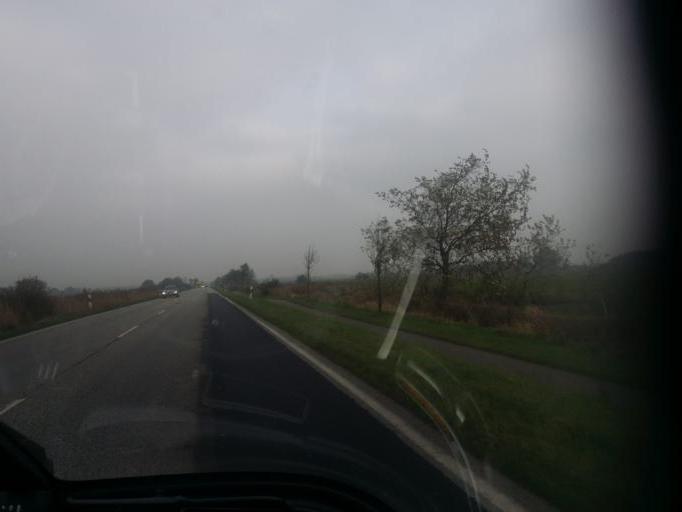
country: DE
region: Schleswig-Holstein
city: Hattstedtermarsch
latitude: 54.5608
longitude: 9.0005
